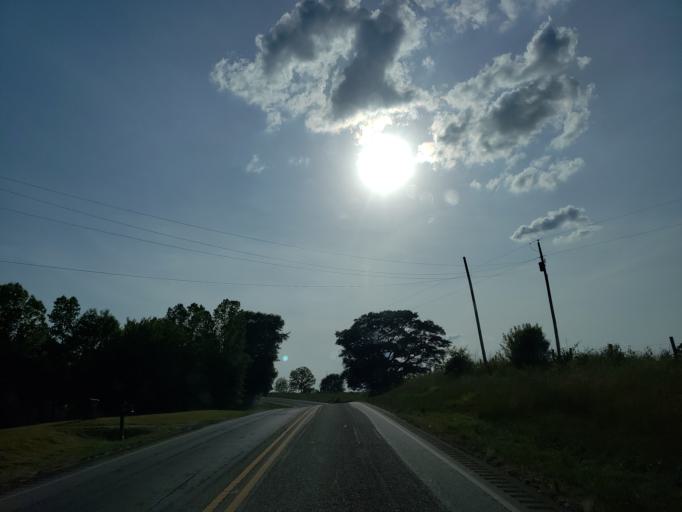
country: US
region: Georgia
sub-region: Carroll County
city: Bowdon
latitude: 33.4653
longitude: -85.3072
